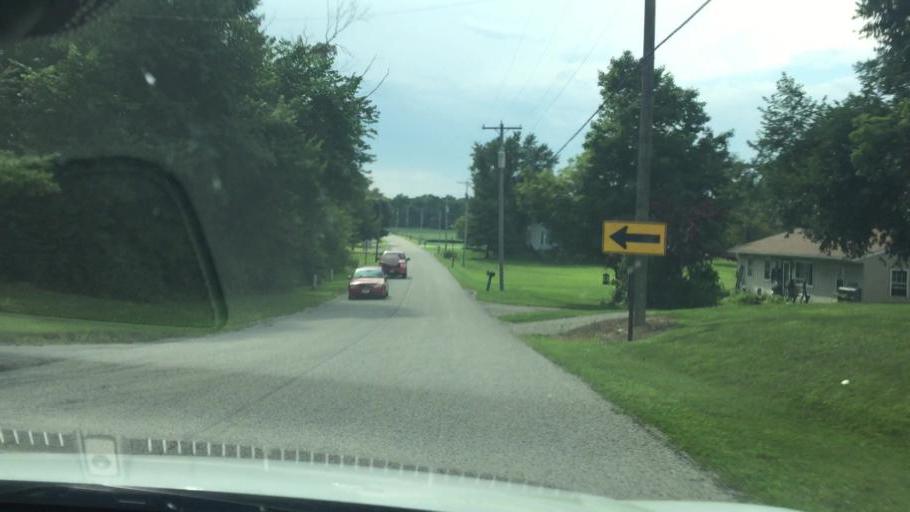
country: US
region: Ohio
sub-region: Clark County
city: Lisbon
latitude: 39.9453
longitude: -83.5986
